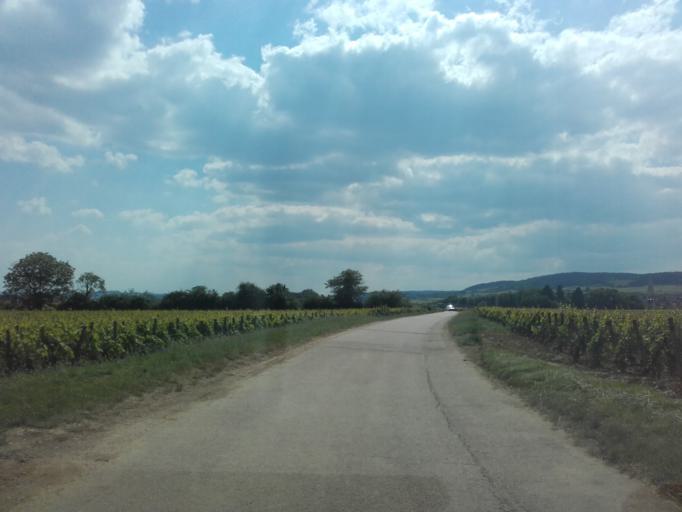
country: FR
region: Bourgogne
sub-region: Departement de la Cote-d'Or
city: Meursault
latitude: 46.9816
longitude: 4.7836
